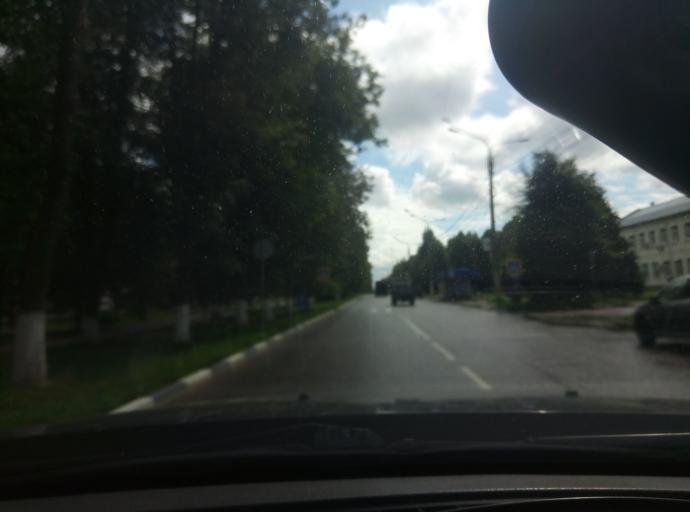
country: RU
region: Tula
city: Novomoskovsk
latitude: 54.0147
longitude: 38.2961
